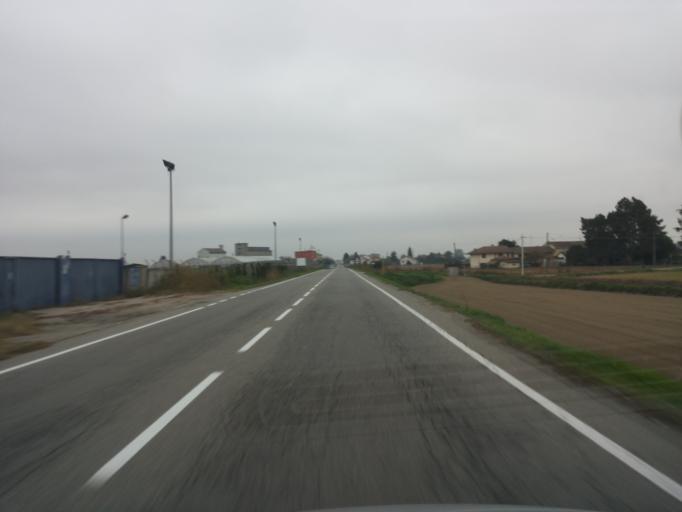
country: IT
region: Piedmont
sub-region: Provincia di Vercelli
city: Borgo Vercelli
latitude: 45.3312
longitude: 8.4485
